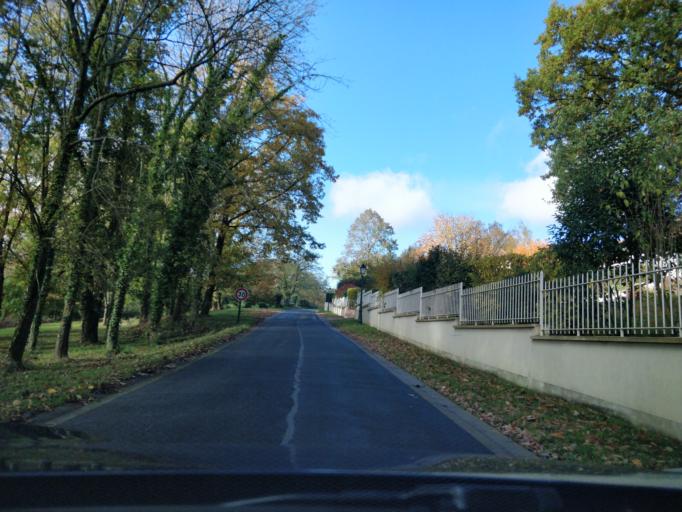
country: FR
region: Ile-de-France
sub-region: Departement de l'Essonne
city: Fontenay-les-Briis
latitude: 48.6316
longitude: 2.1601
